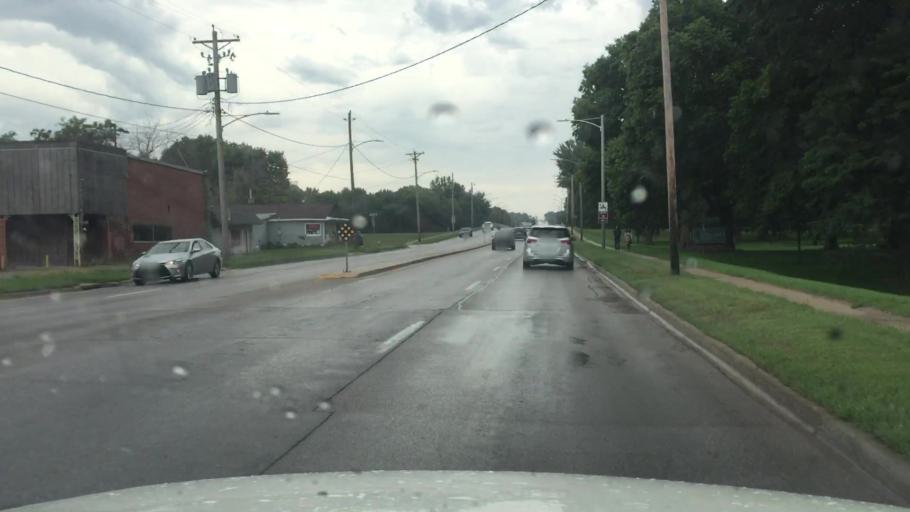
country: US
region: Iowa
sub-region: Polk County
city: Des Moines
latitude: 41.5790
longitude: -93.5970
